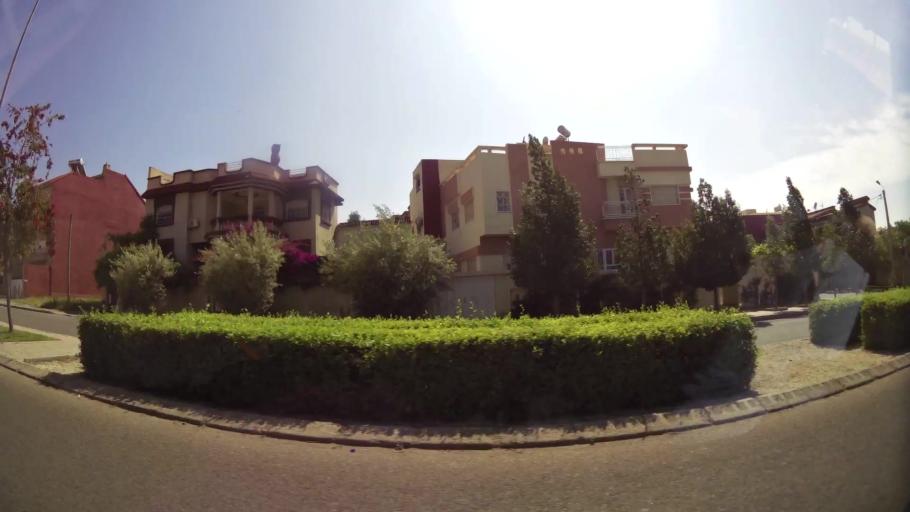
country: MA
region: Oriental
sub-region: Oujda-Angad
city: Oujda
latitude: 34.6933
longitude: -1.8803
